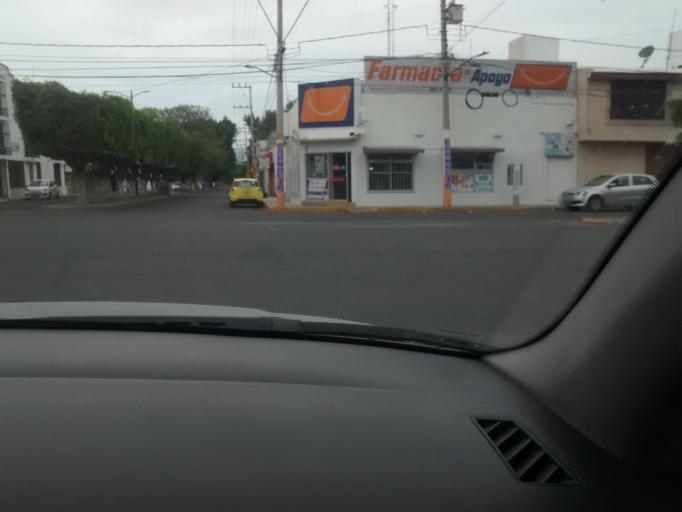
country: MX
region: Puebla
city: Tehuacan
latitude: 18.4613
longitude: -97.4096
